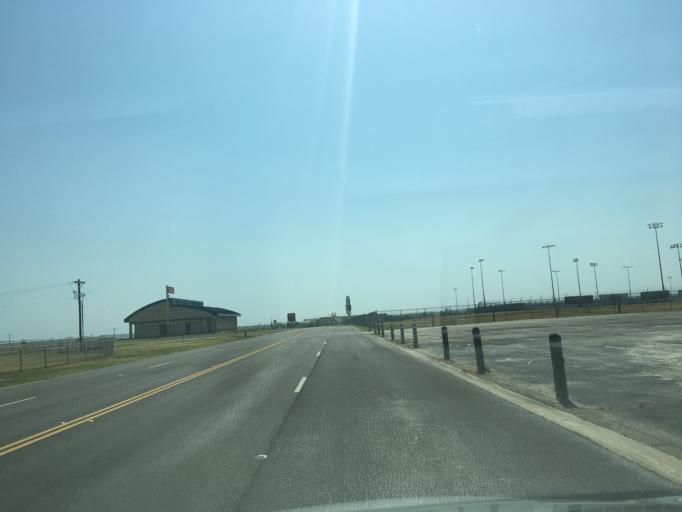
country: US
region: Texas
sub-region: Denton County
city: Justin
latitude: 33.0353
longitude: -97.2760
